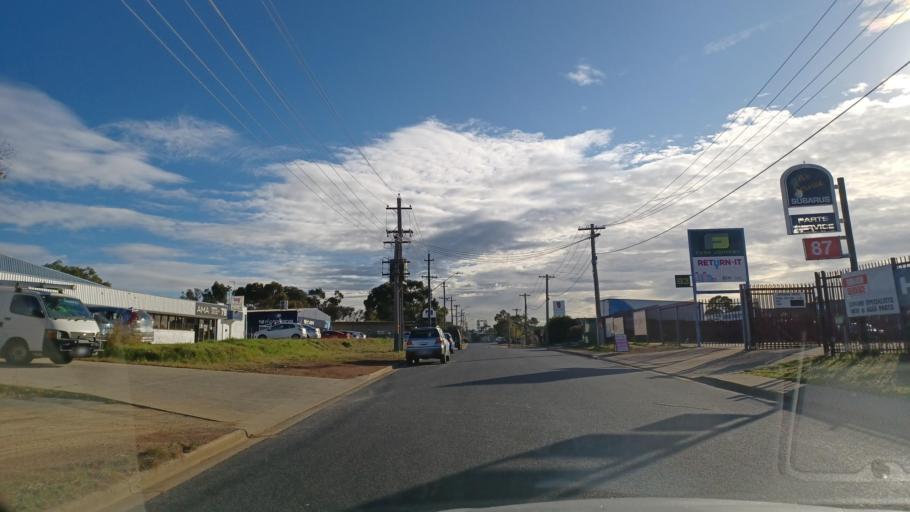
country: AU
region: Australian Capital Territory
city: Kaleen
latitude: -35.2196
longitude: 149.1379
